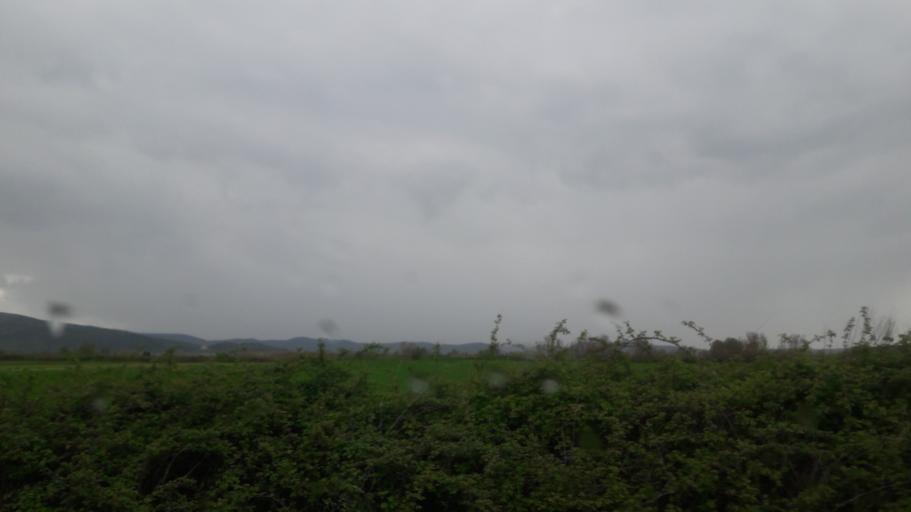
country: AL
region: Shkoder
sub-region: Rrethi i Shkodres
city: Berdica e Madhe
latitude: 41.9633
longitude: 19.5020
